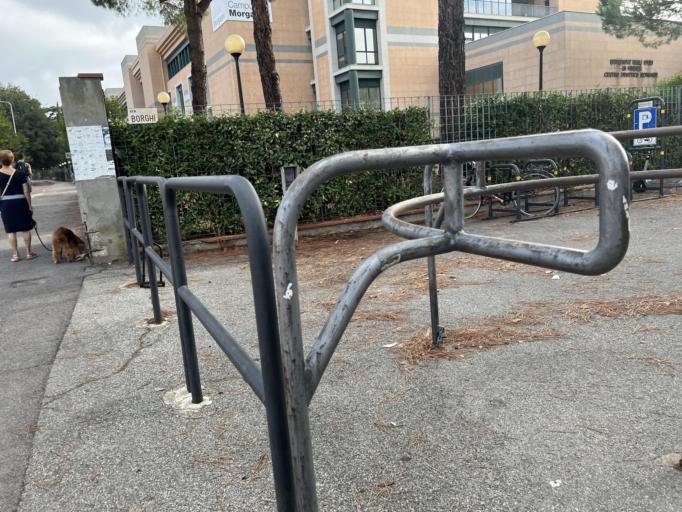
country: IT
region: Tuscany
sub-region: Province of Florence
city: Florence
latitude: 43.8003
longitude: 11.2446
